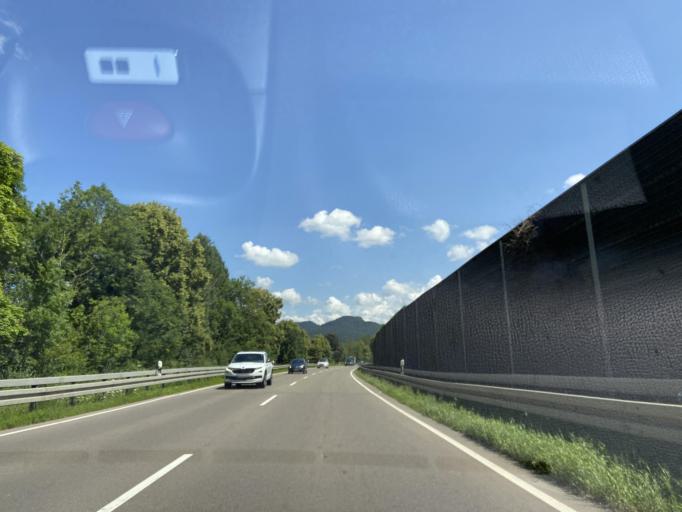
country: DE
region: Baden-Wuerttemberg
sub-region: Tuebingen Region
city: Balingen
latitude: 48.2426
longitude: 8.8660
